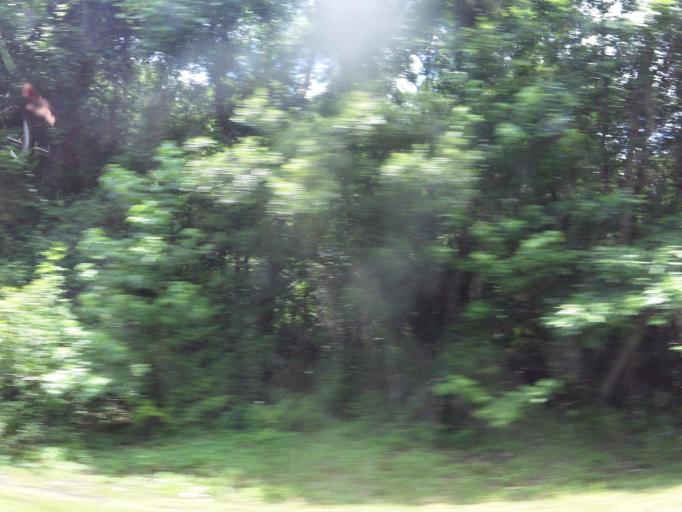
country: US
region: Florida
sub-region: Clay County
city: Green Cove Springs
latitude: 29.9457
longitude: -81.7422
